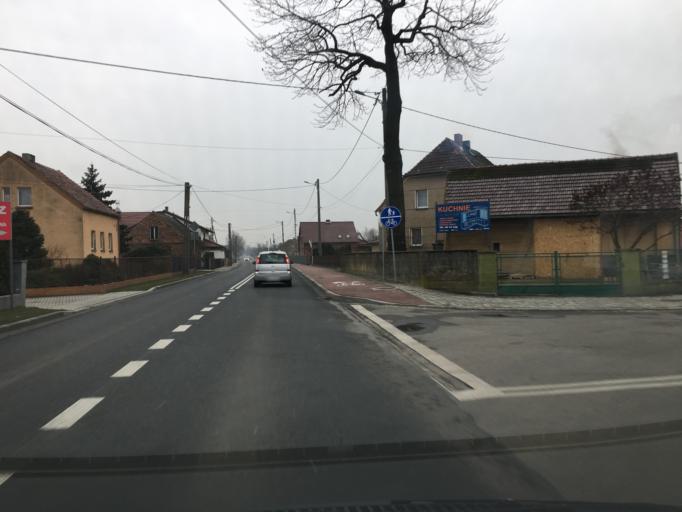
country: PL
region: Opole Voivodeship
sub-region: Powiat kedzierzynsko-kozielski
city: Kedzierzyn-Kozle
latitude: 50.3148
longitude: 18.2252
